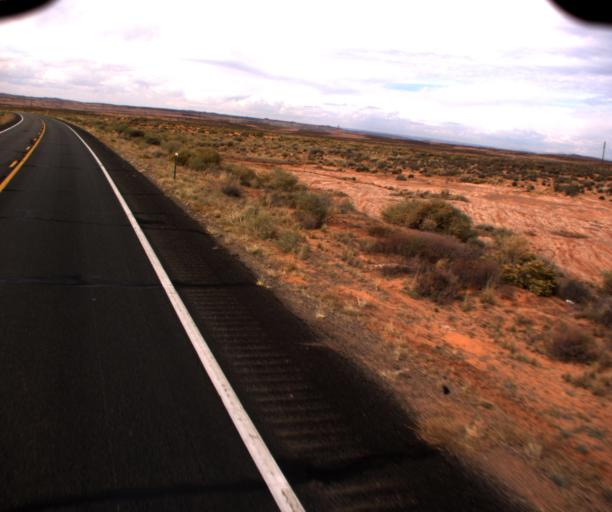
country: US
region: Arizona
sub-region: Apache County
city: Many Farms
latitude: 36.9393
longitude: -109.6400
